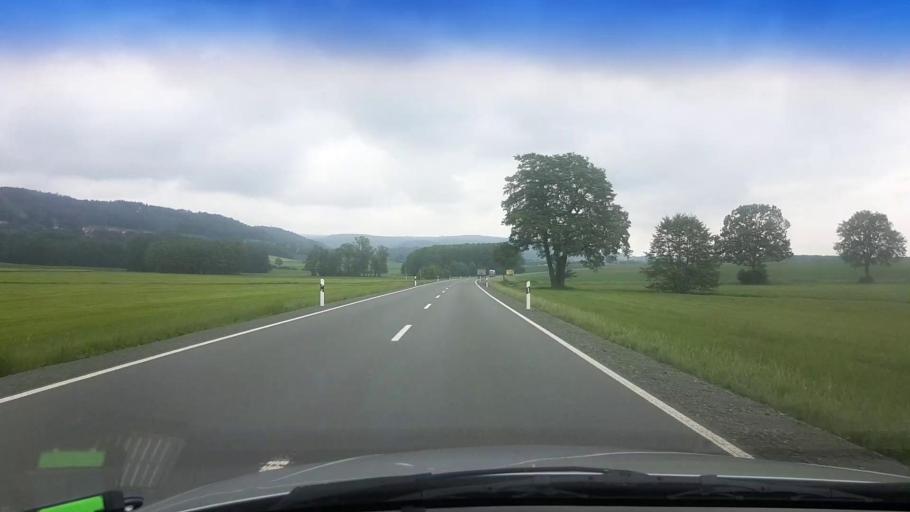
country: DE
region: Bavaria
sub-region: Upper Franconia
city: Gesees
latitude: 50.0264
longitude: 11.6593
